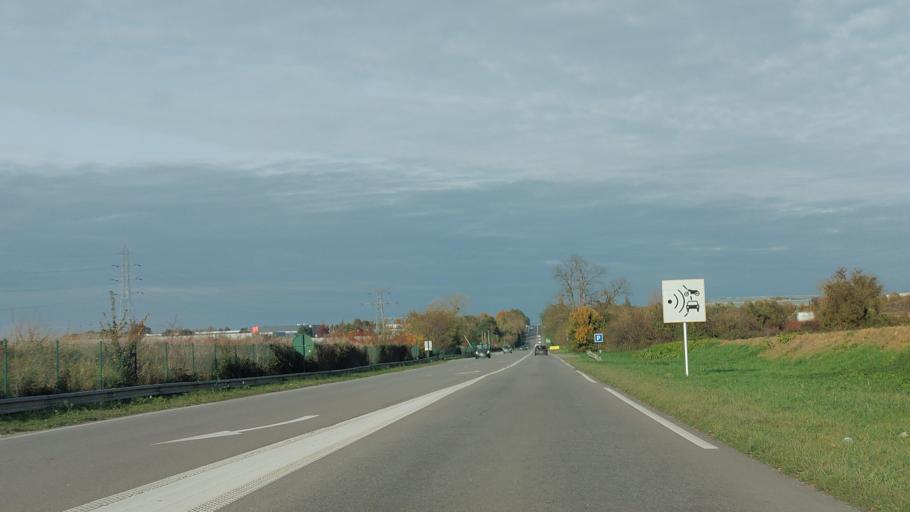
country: FR
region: Ile-de-France
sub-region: Departement du Val-d'Oise
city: Survilliers
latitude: 49.0817
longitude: 2.5296
